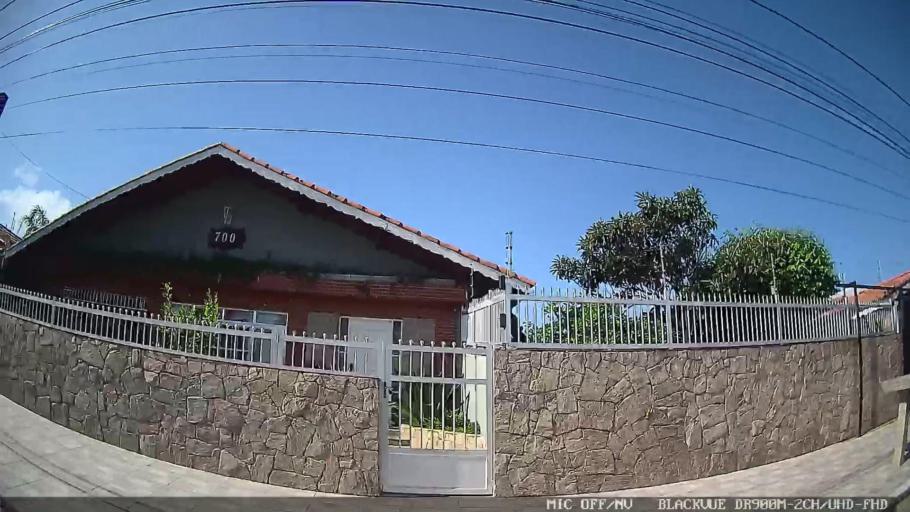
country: BR
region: Sao Paulo
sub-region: Peruibe
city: Peruibe
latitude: -24.3070
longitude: -46.9884
